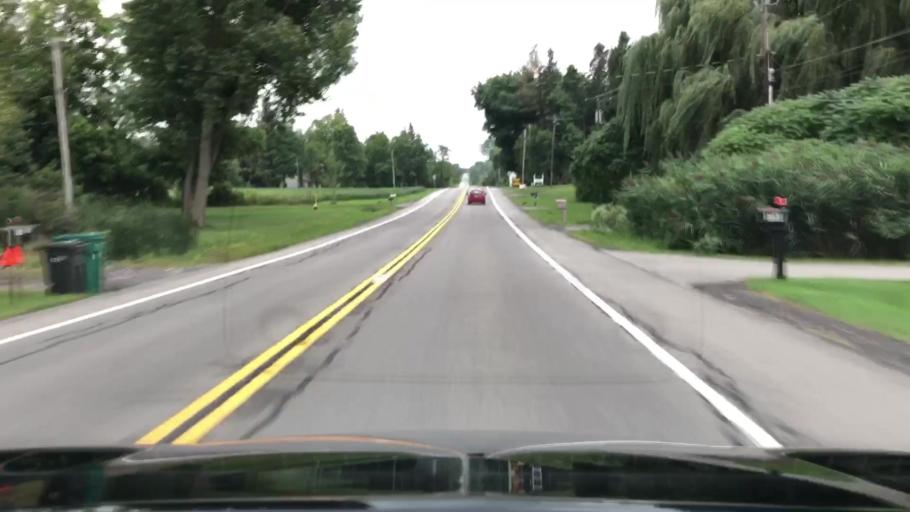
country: US
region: New York
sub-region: Erie County
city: Orchard Park
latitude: 42.7826
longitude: -78.6970
